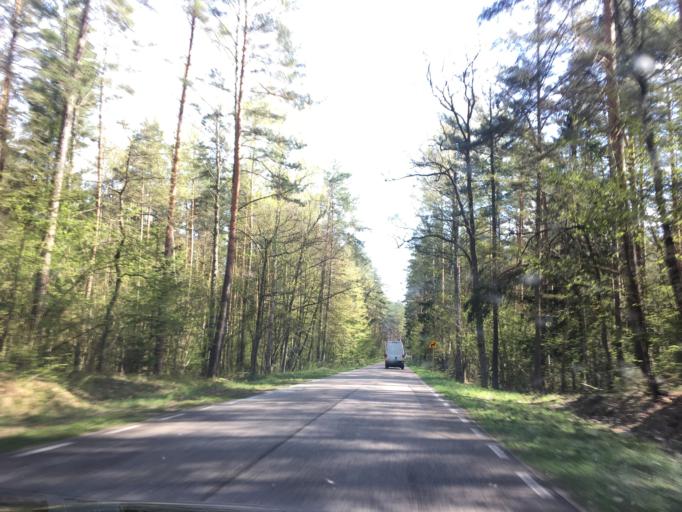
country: PL
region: Warmian-Masurian Voivodeship
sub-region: Powiat piski
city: Ruciane-Nida
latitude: 53.6752
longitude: 21.5835
